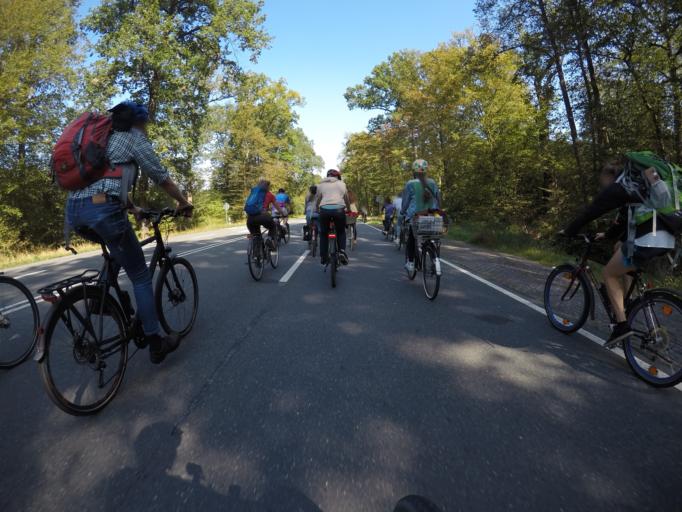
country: DE
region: Hesse
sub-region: Regierungsbezirk Darmstadt
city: Offenbach
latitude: 50.0715
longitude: 8.7359
